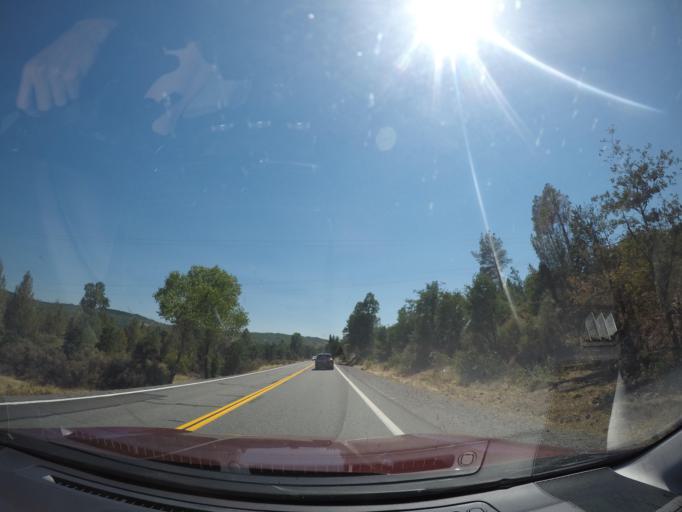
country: US
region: California
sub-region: Shasta County
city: Burney
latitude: 40.7993
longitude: -121.9392
